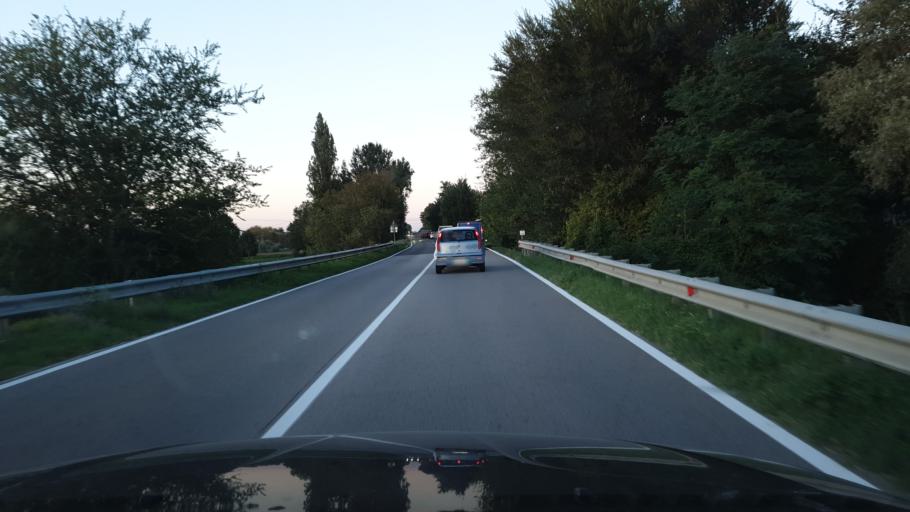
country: IT
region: Emilia-Romagna
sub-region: Provincia di Bologna
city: Ca De Fabbri
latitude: 44.5998
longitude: 11.4388
